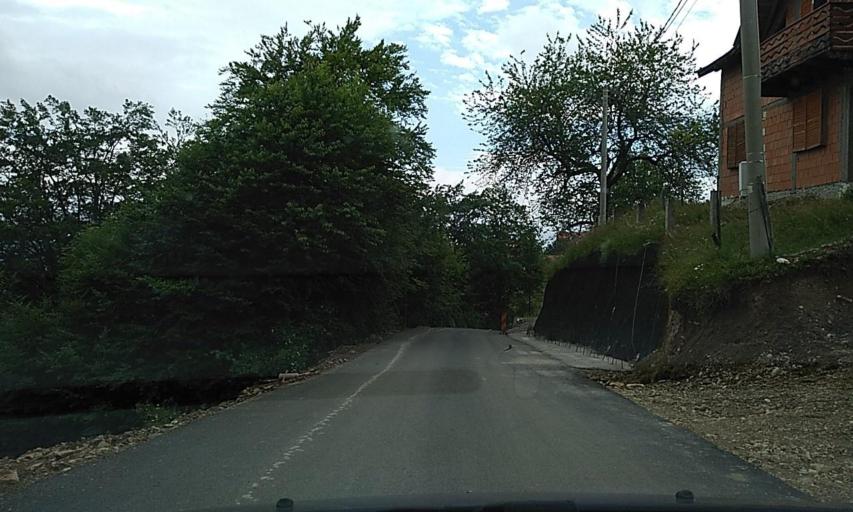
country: RO
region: Hunedoara
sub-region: Oras Petrila
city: Petrila
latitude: 45.3906
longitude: 23.4466
